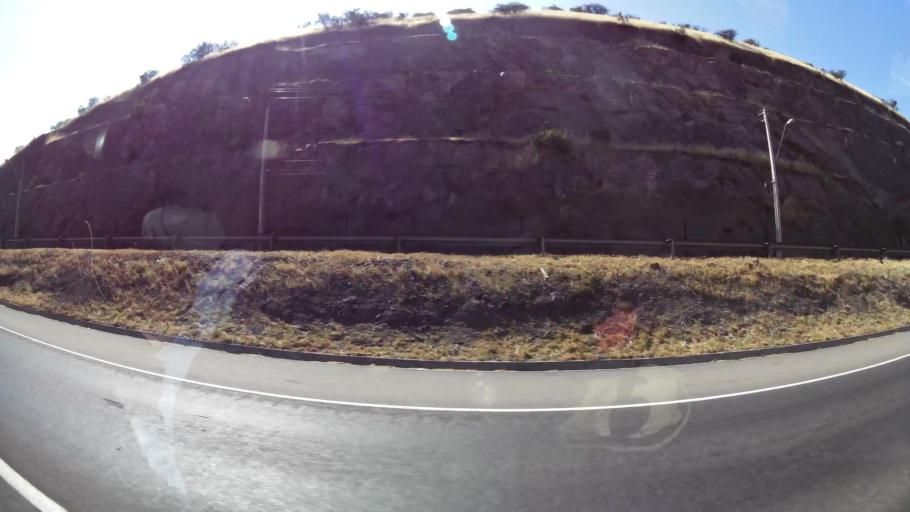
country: CL
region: Santiago Metropolitan
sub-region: Provincia de Chacabuco
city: Chicureo Abajo
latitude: -33.3503
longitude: -70.6936
